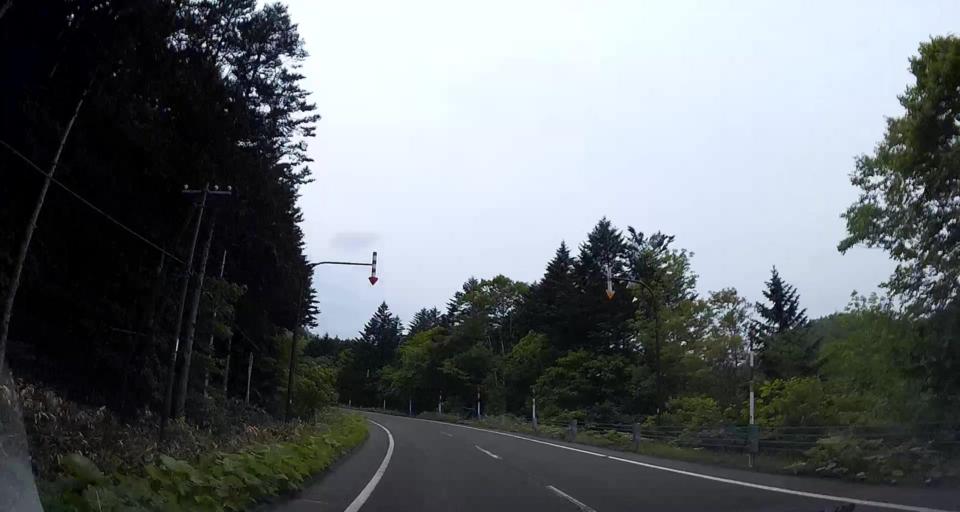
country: JP
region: Hokkaido
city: Shiraoi
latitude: 42.6497
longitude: 141.2051
